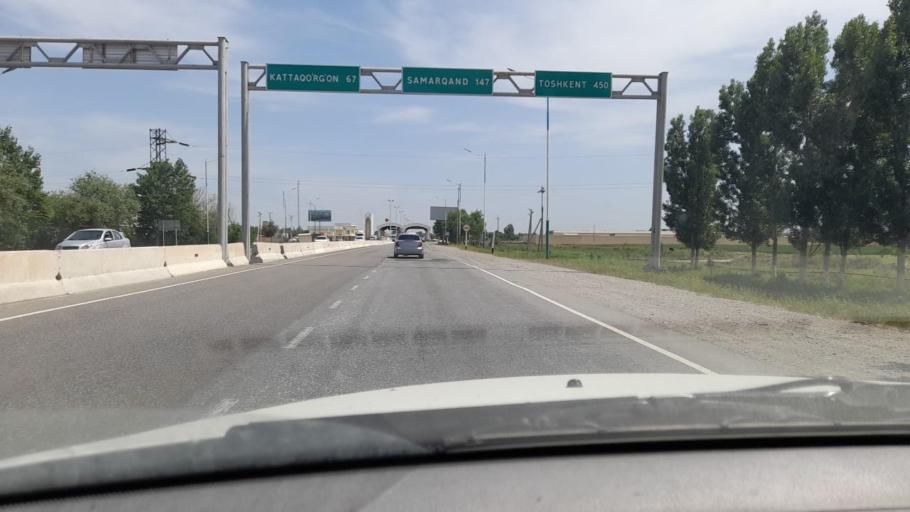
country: UZ
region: Navoiy
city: Karmana Shahri
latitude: 40.1199
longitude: 65.4856
